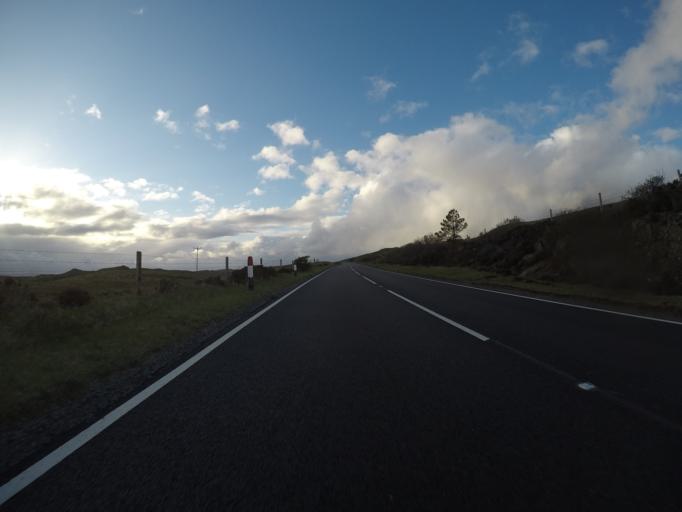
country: GB
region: Scotland
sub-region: Highland
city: Portree
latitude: 57.5359
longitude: -6.3612
